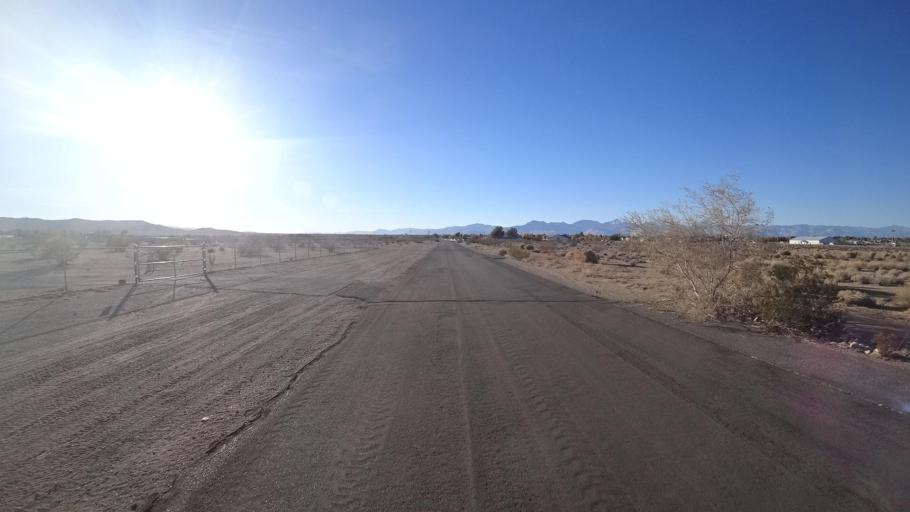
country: US
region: California
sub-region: Kern County
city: Ridgecrest
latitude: 35.6009
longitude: -117.6654
